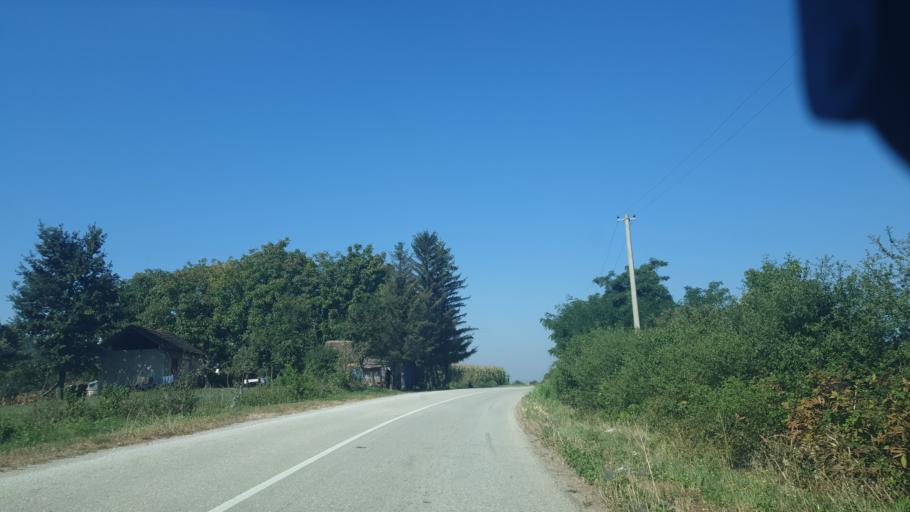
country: RS
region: Central Serbia
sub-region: Kolubarski Okrug
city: Lajkovac
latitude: 44.3034
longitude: 20.1392
